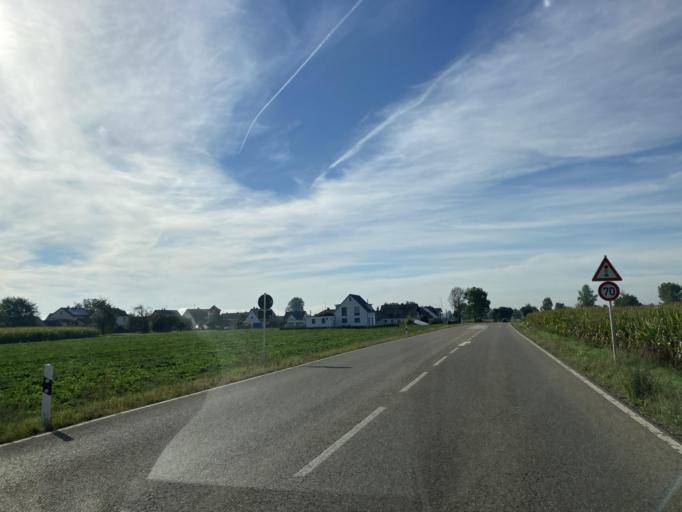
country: DE
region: Baden-Wuerttemberg
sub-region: Regierungsbezirk Stuttgart
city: Niederstotzingen
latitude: 48.5101
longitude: 10.2506
